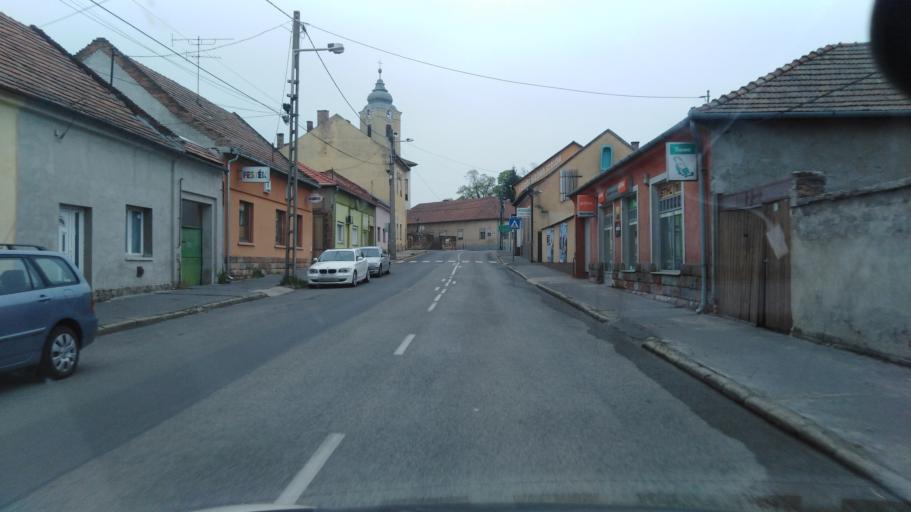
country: HU
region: Nograd
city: Balassagyarmat
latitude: 48.0773
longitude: 19.2956
